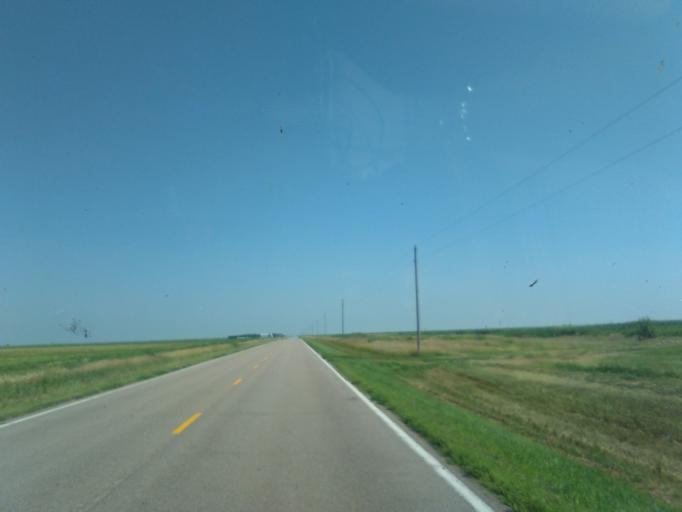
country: US
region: Nebraska
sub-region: Dundy County
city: Benkelman
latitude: 39.8158
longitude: -101.5415
